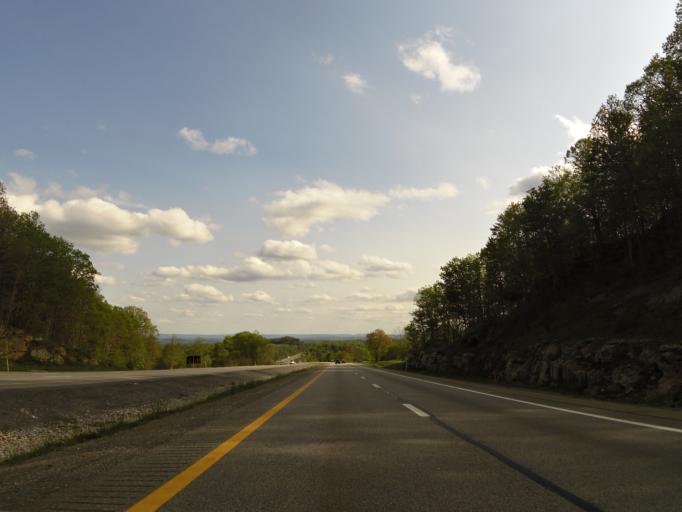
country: US
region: West Virginia
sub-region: Raleigh County
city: Shady Spring
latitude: 37.5654
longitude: -81.1128
